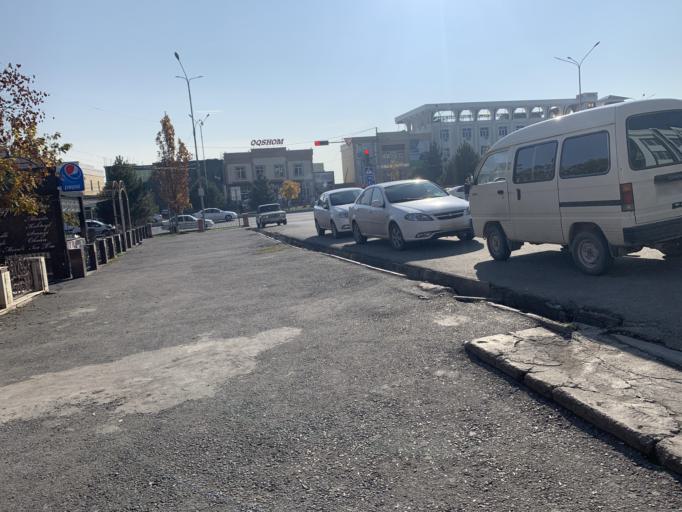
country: UZ
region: Namangan
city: Namangan Shahri
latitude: 40.9964
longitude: 71.5905
